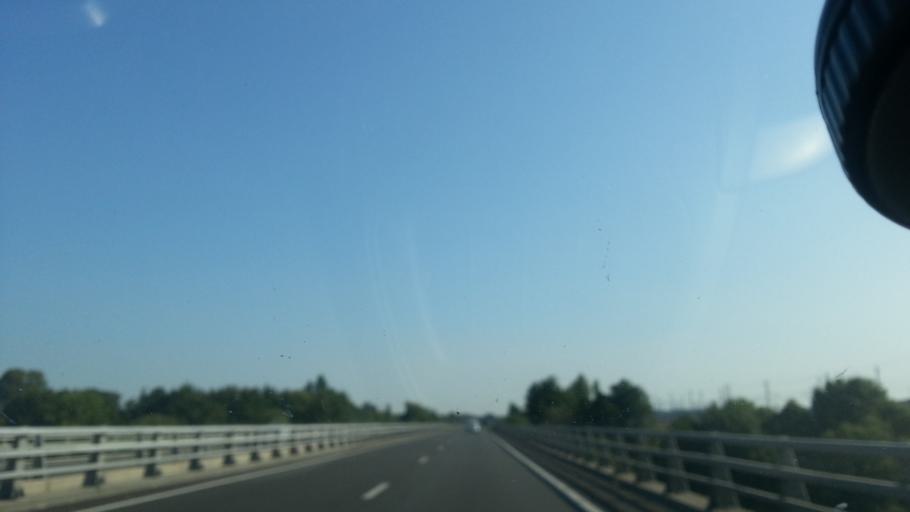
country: FR
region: Centre
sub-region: Departement d'Indre-et-Loire
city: La Celle-Saint-Avant
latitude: 47.0166
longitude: 0.5618
